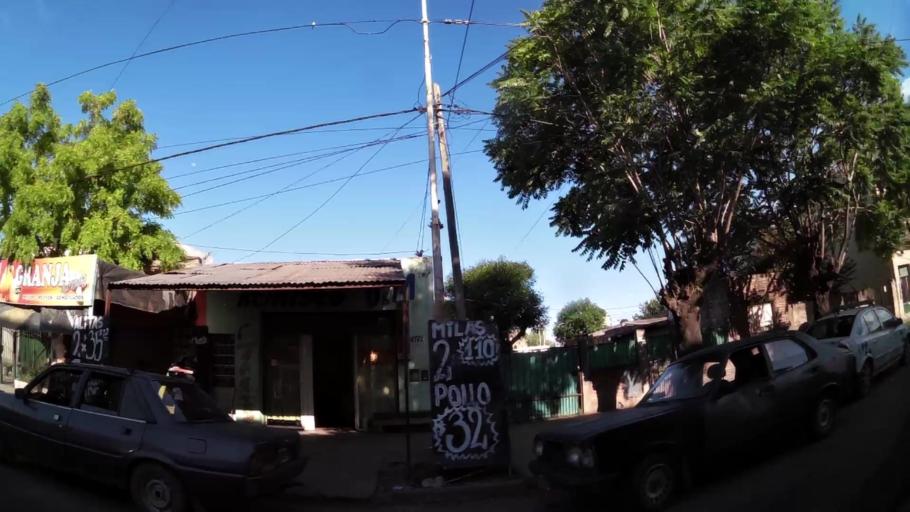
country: AR
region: Buenos Aires
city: Santa Catalina - Dique Lujan
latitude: -34.4971
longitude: -58.7287
